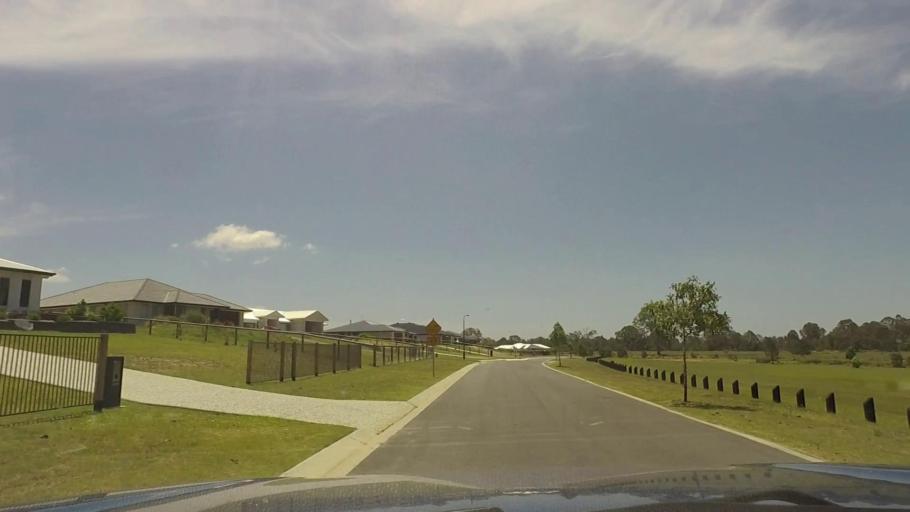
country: AU
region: Queensland
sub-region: Logan
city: Chambers Flat
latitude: -27.7723
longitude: 153.0929
